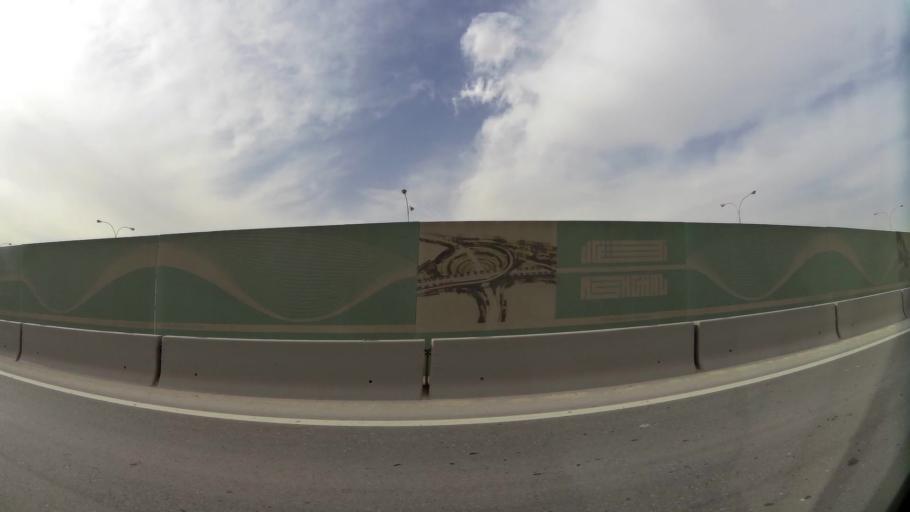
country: QA
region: Baladiyat ar Rayyan
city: Ar Rayyan
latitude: 25.3107
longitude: 51.4114
